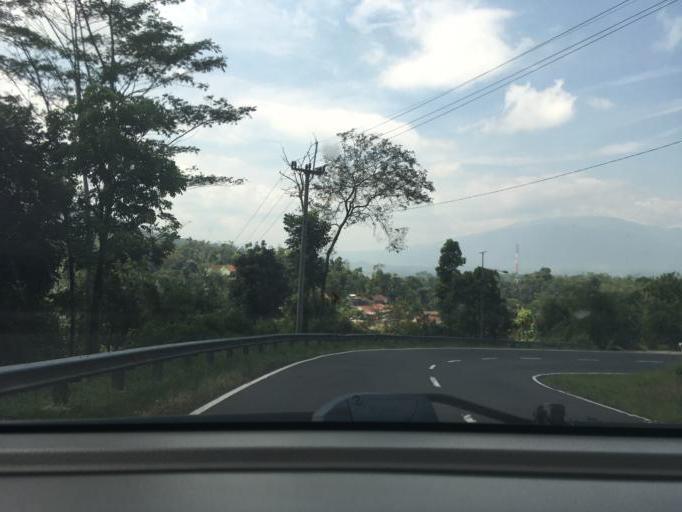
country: ID
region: West Java
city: Wage Cibahayu
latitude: -7.1144
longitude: 108.1162
